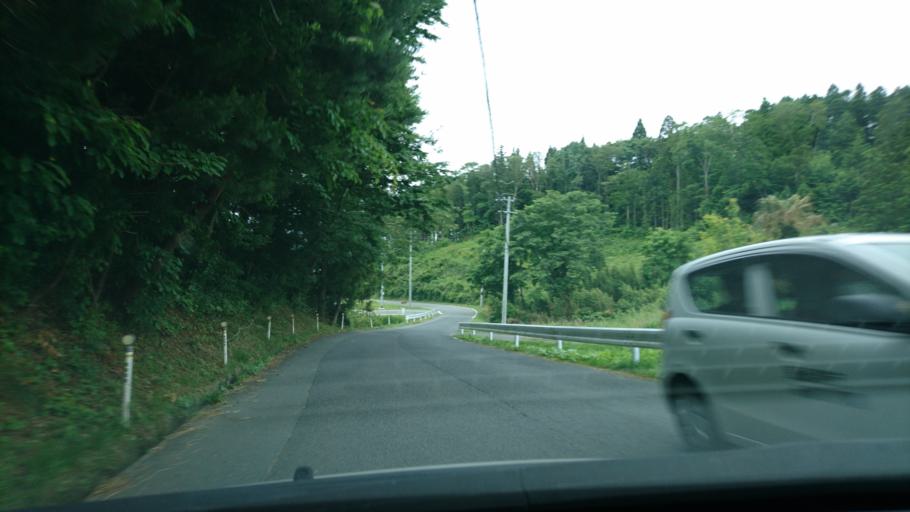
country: JP
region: Miyagi
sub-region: Oshika Gun
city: Onagawa Cho
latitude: 38.7775
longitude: 141.5132
